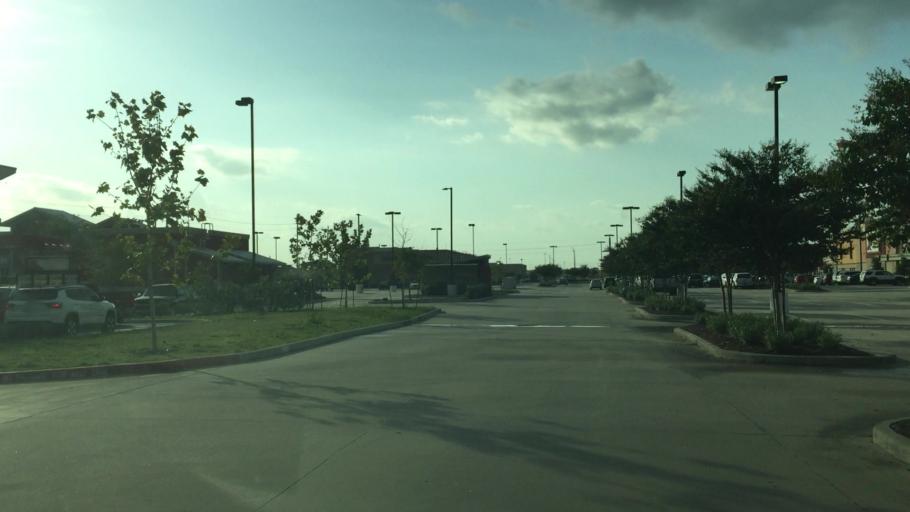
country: US
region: Texas
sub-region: Montgomery County
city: The Woodlands
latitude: 30.0791
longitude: -95.5175
